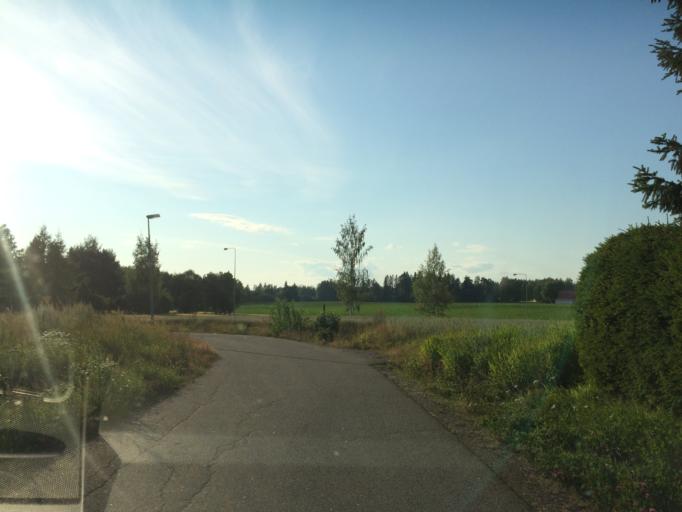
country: FI
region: Haeme
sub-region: Haemeenlinna
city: Parola
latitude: 61.0460
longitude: 24.3788
